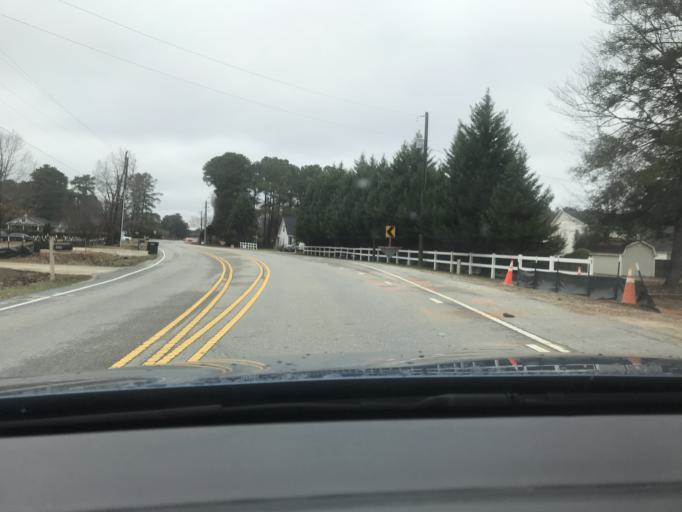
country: US
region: North Carolina
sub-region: Hoke County
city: Rockfish
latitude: 35.0313
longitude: -79.0061
